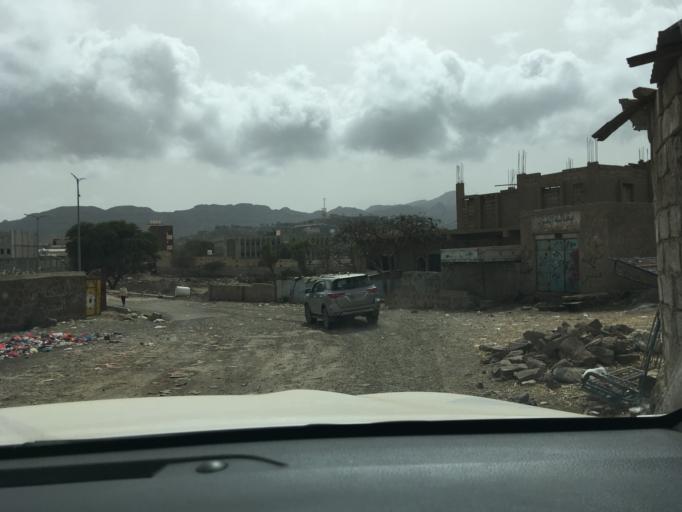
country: YE
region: Ad Dali'
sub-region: Ad Dhale'e
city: Dhalie
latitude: 13.7064
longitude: 44.7368
